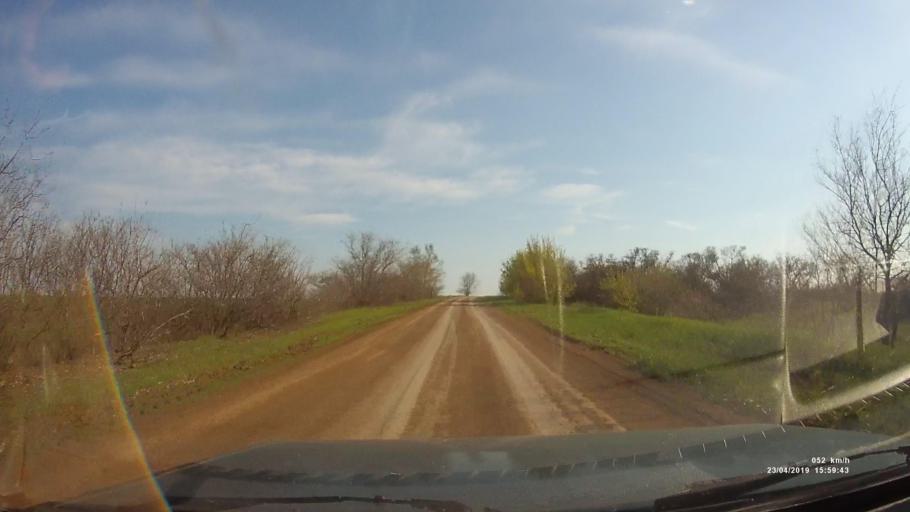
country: RU
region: Rostov
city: Remontnoye
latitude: 46.5147
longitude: 43.1095
